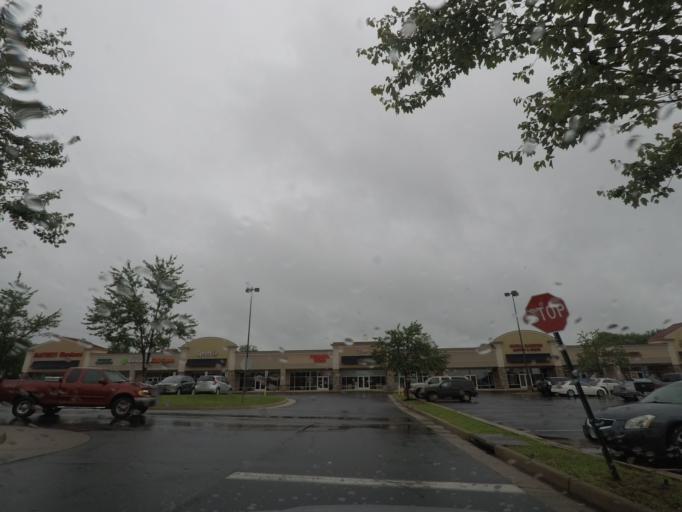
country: US
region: Virginia
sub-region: Culpeper County
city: Culpeper
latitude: 38.4863
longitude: -77.9694
